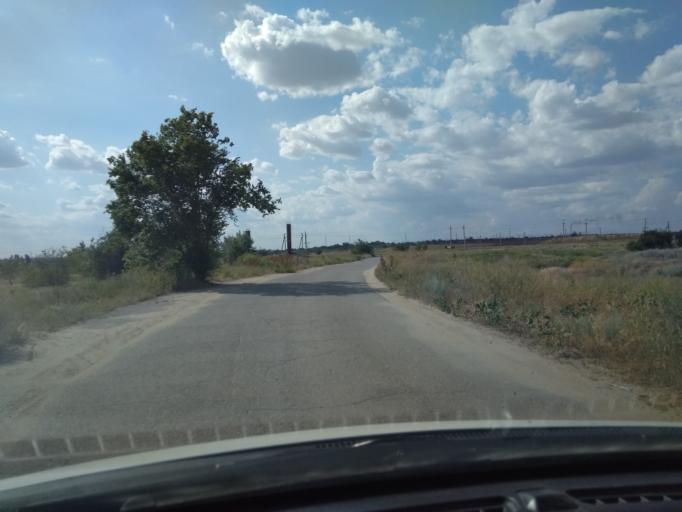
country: RU
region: Volgograd
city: Vodstroy
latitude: 48.8037
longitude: 44.5302
